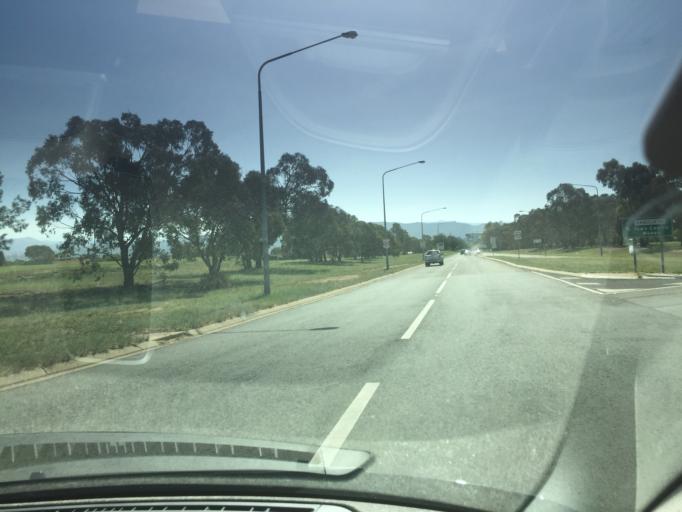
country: AU
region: Australian Capital Territory
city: Macarthur
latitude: -35.4239
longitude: 149.0896
